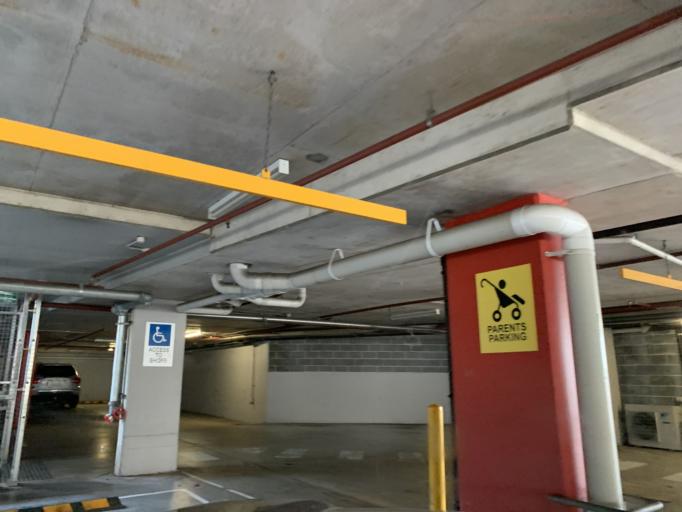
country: AU
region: New South Wales
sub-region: Hornsby Shire
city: Galston
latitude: -33.6526
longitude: 151.0462
